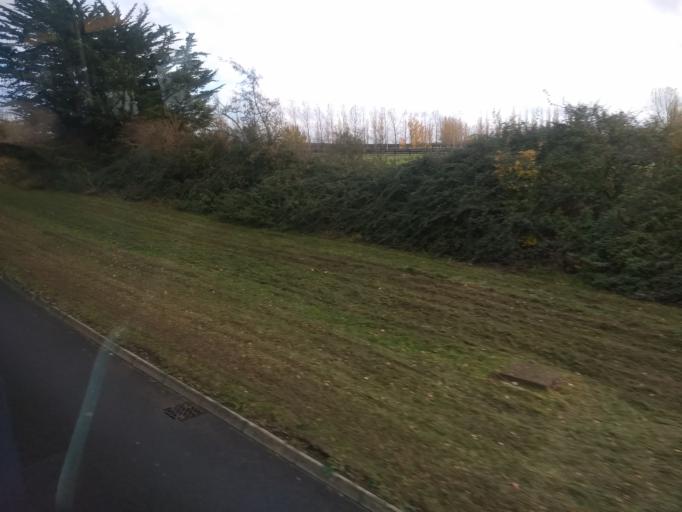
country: GB
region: England
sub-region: Isle of Wight
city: Shalfleet
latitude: 50.7028
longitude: -1.3571
